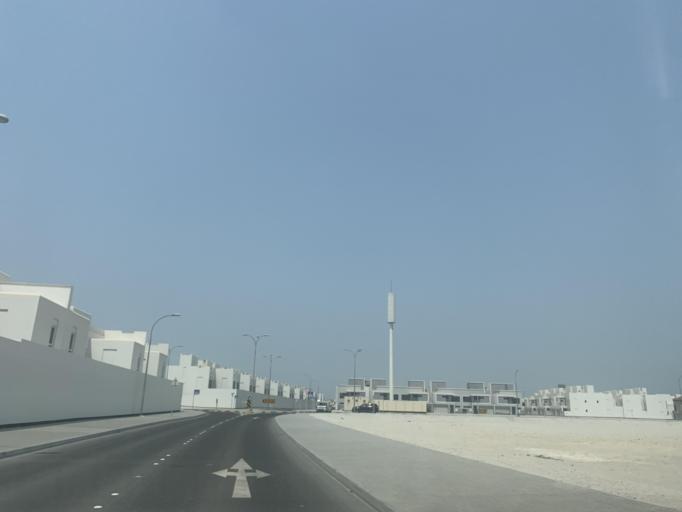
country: BH
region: Muharraq
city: Al Muharraq
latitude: 26.3139
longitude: 50.6217
